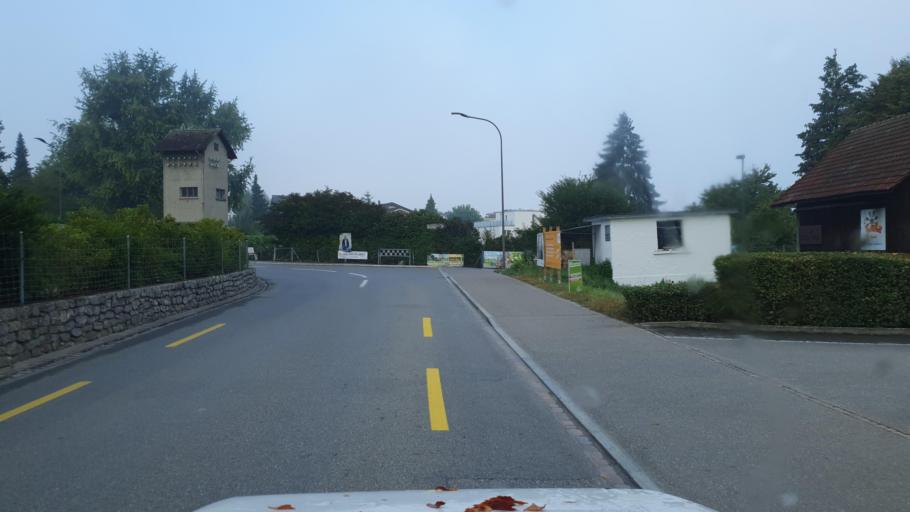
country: CH
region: Aargau
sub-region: Bezirk Baden
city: Mellingen
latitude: 47.4387
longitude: 8.2706
